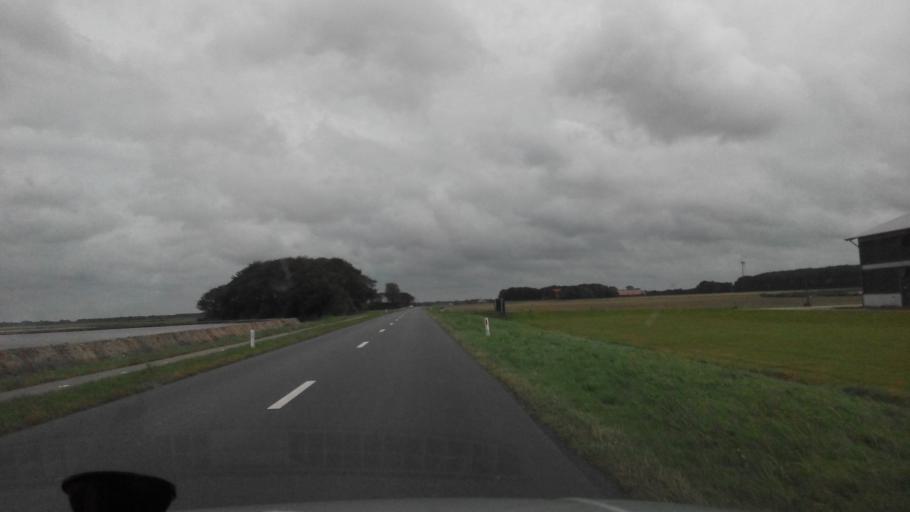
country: NL
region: North Holland
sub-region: Gemeente Hollands Kroon
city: Den Oever
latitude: 52.8720
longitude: 4.9473
